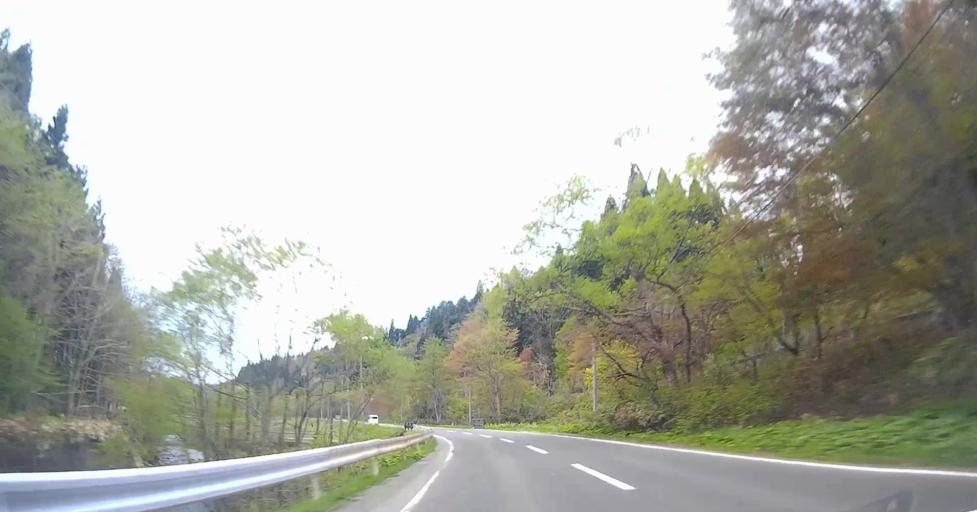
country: JP
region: Aomori
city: Goshogawara
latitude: 41.1258
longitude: 140.5195
